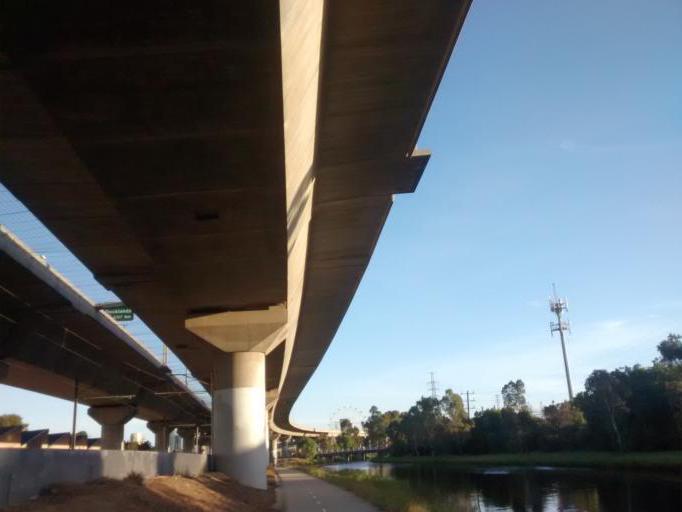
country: AU
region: Victoria
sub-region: Moonee Valley
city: Flemington
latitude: -37.7967
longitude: 144.9359
